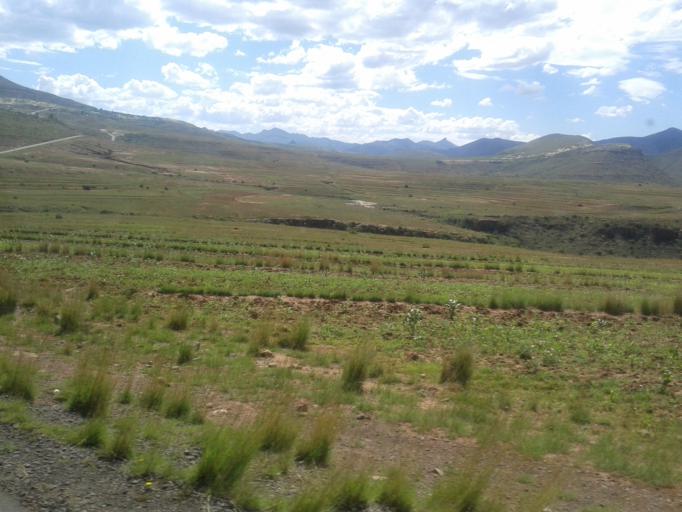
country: LS
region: Qacha's Nek
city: Qacha's Nek
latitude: -30.0380
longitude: 28.3444
